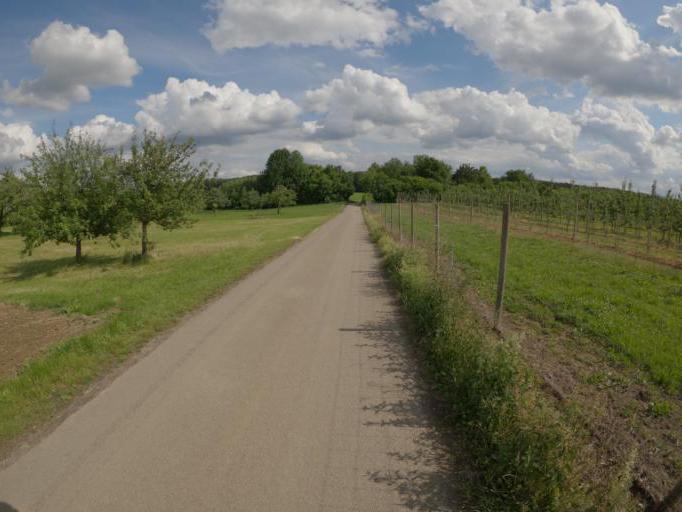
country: DE
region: Baden-Wuerttemberg
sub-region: Regierungsbezirk Stuttgart
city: Hattenhofen
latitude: 48.6613
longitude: 9.5581
